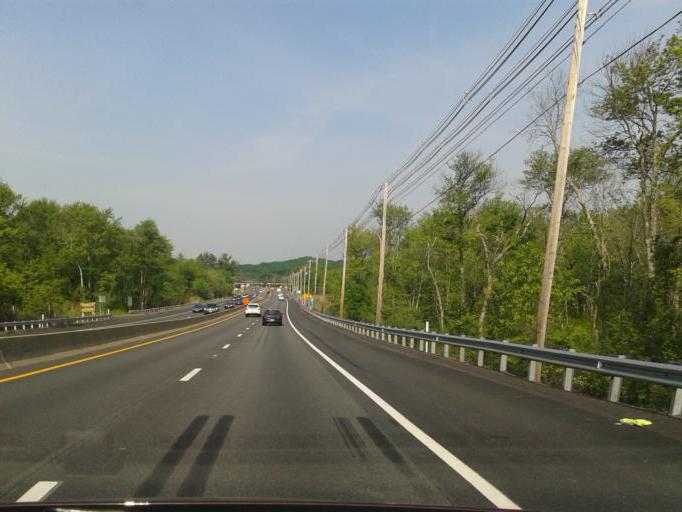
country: US
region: Massachusetts
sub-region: Worcester County
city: Southborough
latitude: 42.2907
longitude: -71.5442
